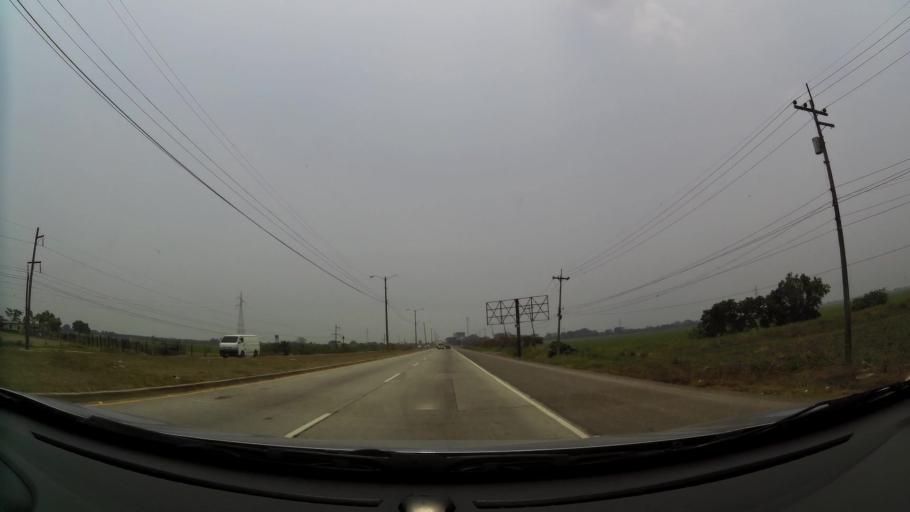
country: HN
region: Yoro
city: El Progreso
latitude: 15.4118
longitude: -87.8596
